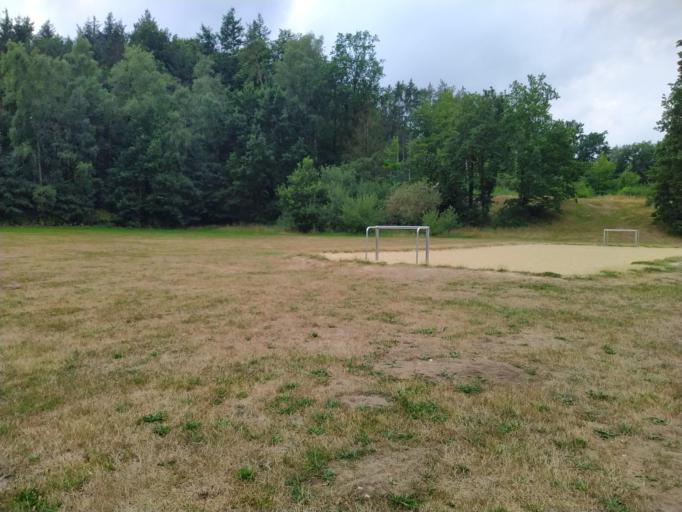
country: DE
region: Lower Saxony
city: Wingst
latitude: 53.7423
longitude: 9.0877
